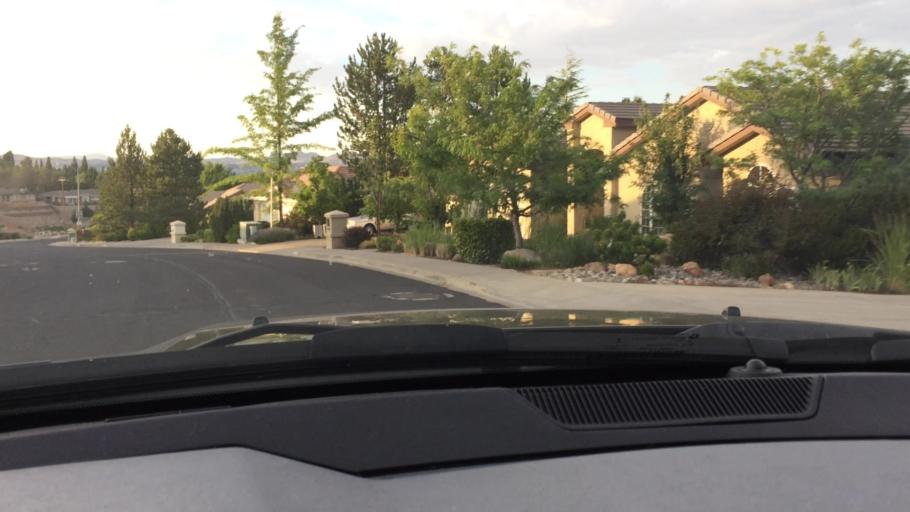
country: US
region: Nevada
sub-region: Washoe County
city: Reno
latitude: 39.4834
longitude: -119.8271
